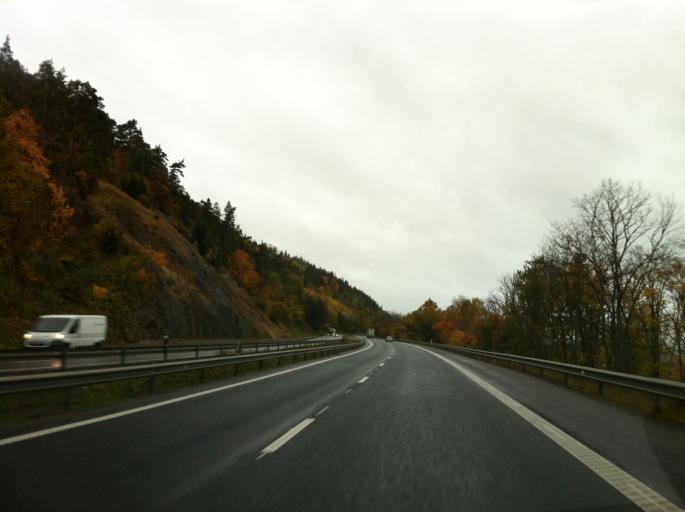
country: SE
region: Joenkoeping
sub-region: Jonkopings Kommun
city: Kaxholmen
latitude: 57.9086
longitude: 14.3024
